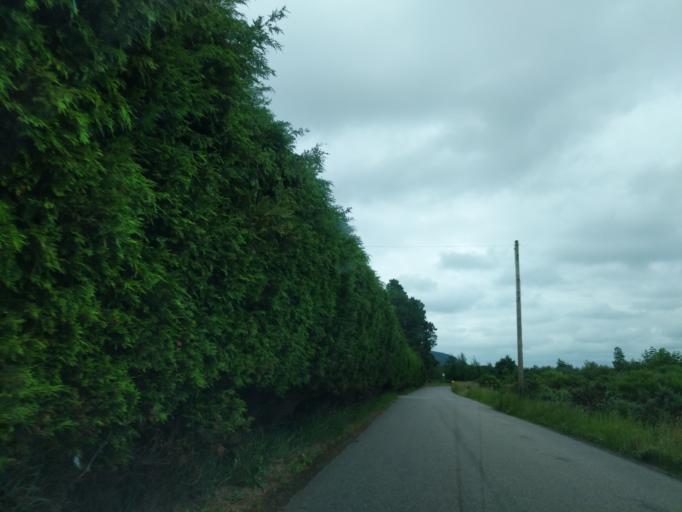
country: GB
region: Scotland
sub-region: Moray
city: Kinloss
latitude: 57.5504
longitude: -3.4992
